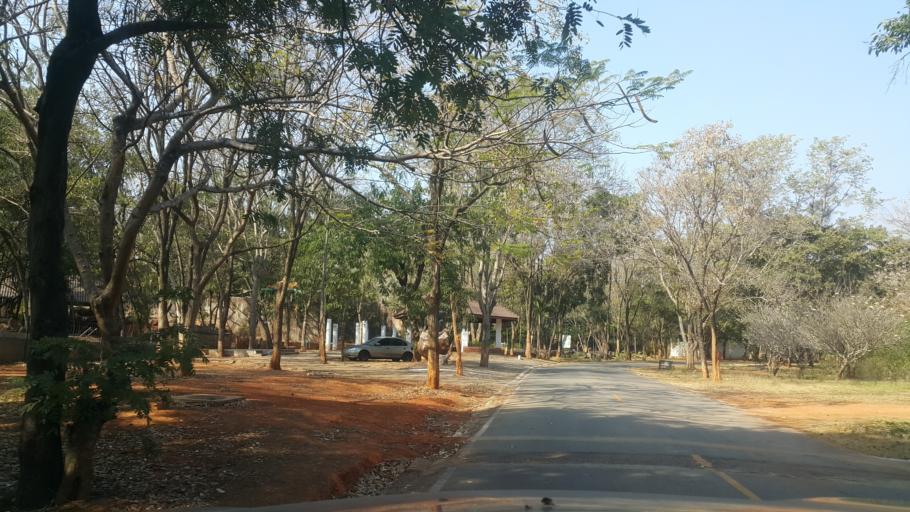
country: TH
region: Nakhon Ratchasima
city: Nakhon Ratchasima
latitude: 14.8519
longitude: 102.0825
